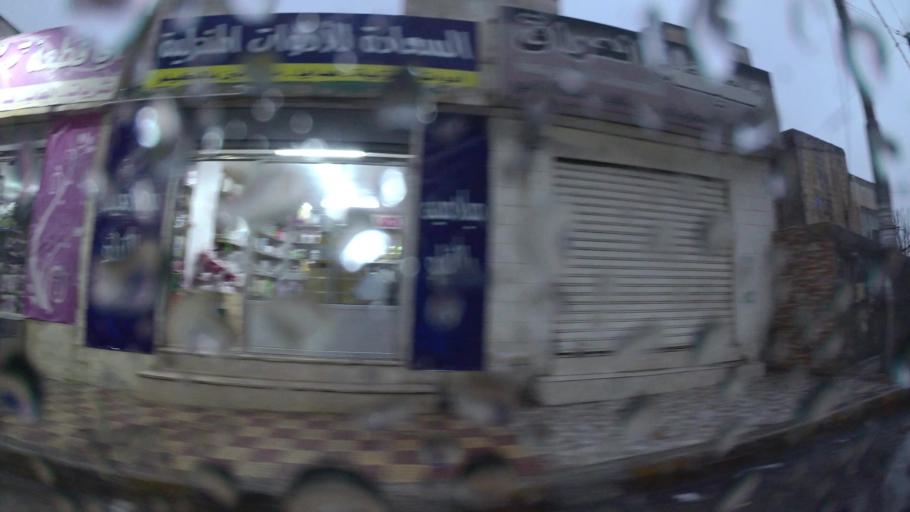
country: JO
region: Amman
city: Al Jubayhah
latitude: 32.0256
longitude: 35.8451
